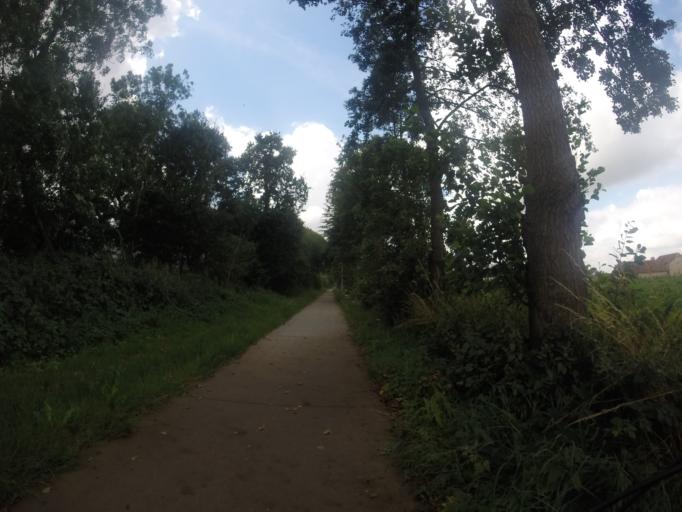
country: BE
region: Flanders
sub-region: Provincie West-Vlaanderen
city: Roeselare
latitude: 50.9241
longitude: 3.0995
